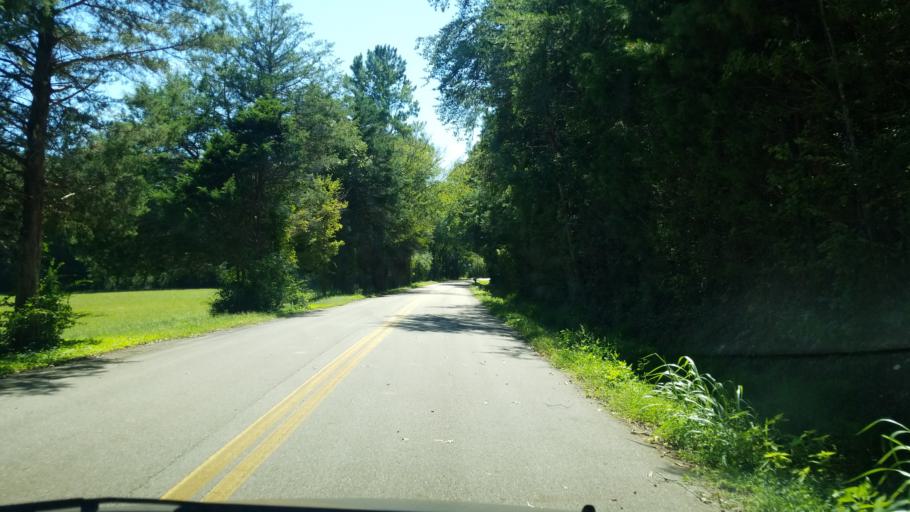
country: US
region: Tennessee
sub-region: Hamilton County
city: Harrison
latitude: 35.1059
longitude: -85.0859
